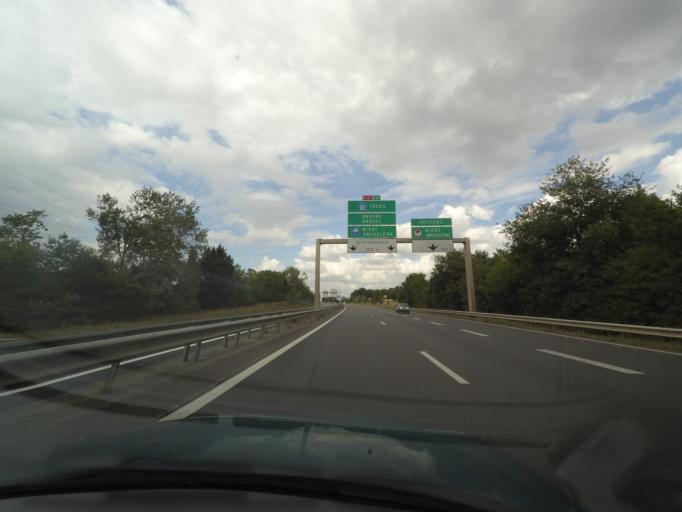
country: FR
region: Poitou-Charentes
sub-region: Departement de la Vienne
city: Mignaloux-Beauvoir
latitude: 46.5679
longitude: 0.3988
